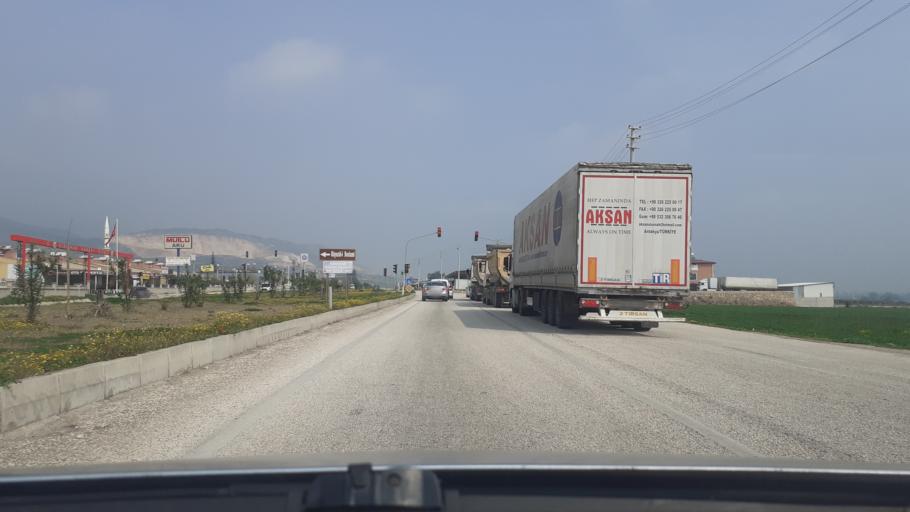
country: TR
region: Hatay
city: Kirikhan
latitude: 36.5226
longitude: 36.3771
